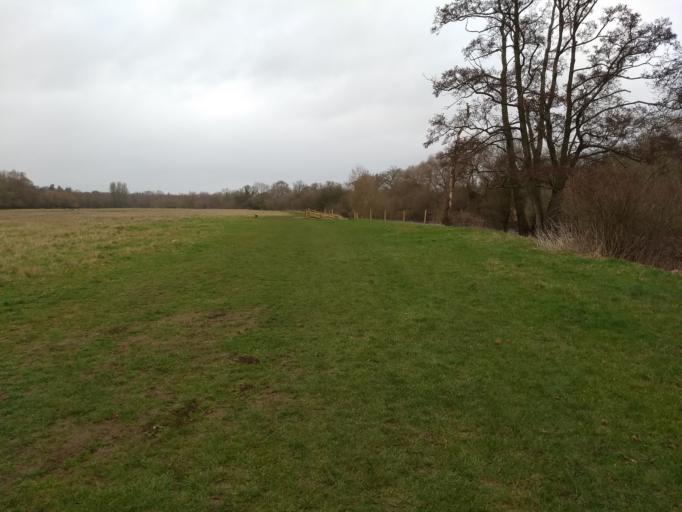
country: GB
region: England
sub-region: Bedford
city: Odell
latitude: 52.2010
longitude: -0.5928
